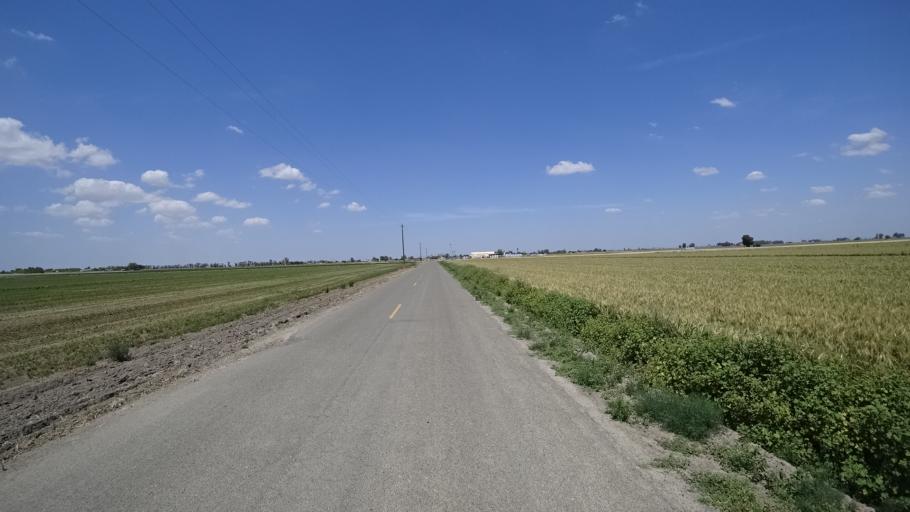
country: US
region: California
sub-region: Kings County
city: Stratford
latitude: 36.1756
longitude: -119.8250
